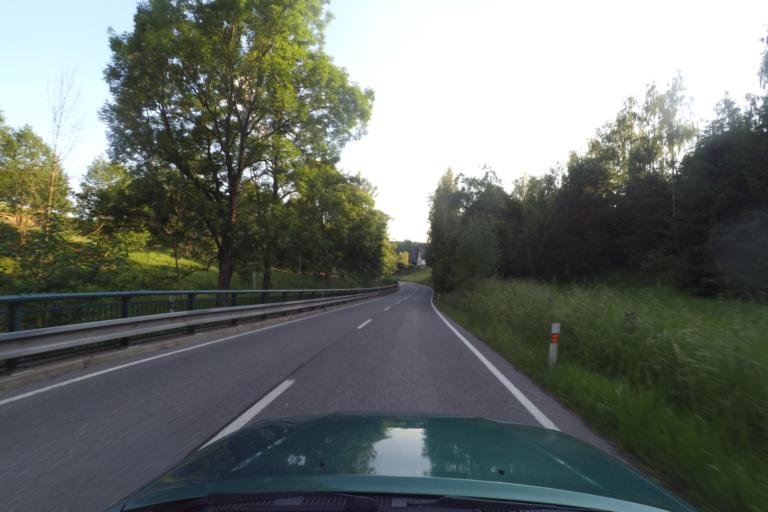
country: CZ
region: Kralovehradecky
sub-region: Okres Trutnov
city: Rudnik
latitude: 50.5923
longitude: 15.7301
